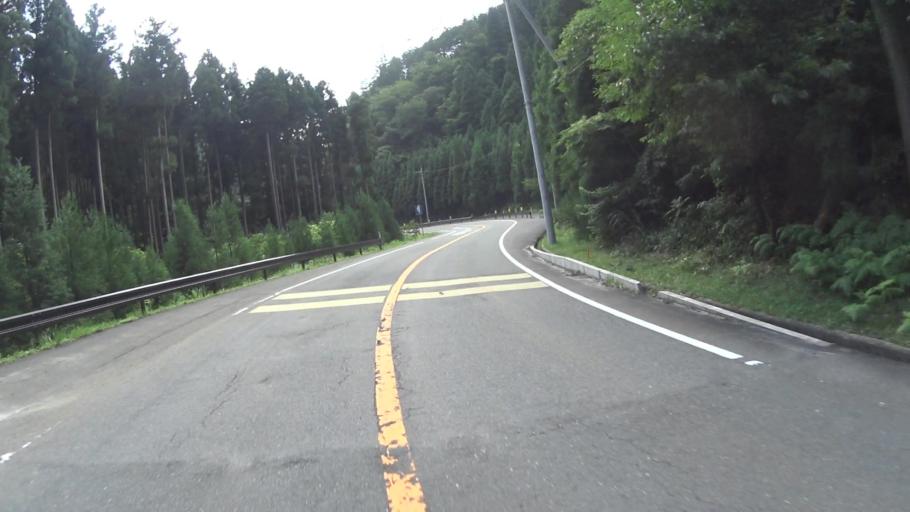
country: JP
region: Fukui
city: Obama
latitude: 35.3428
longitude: 135.5903
